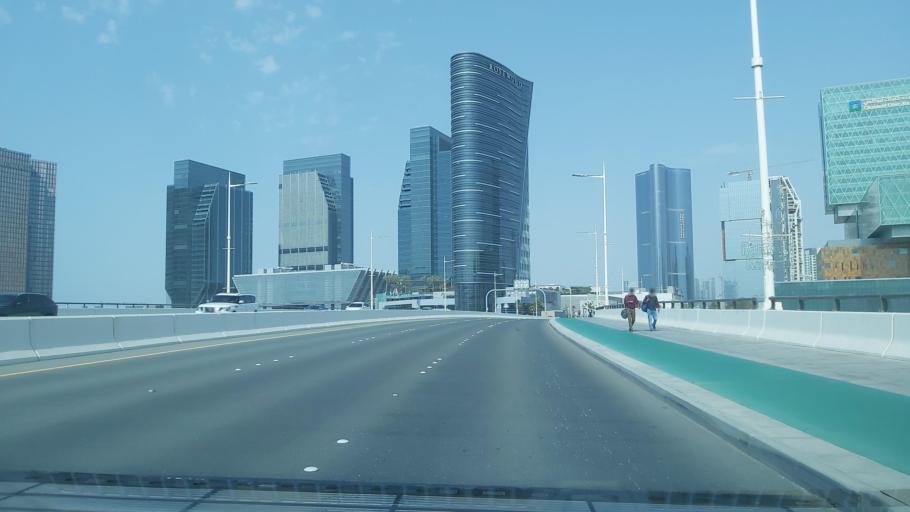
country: AE
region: Abu Dhabi
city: Abu Dhabi
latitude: 24.4988
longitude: 54.3839
